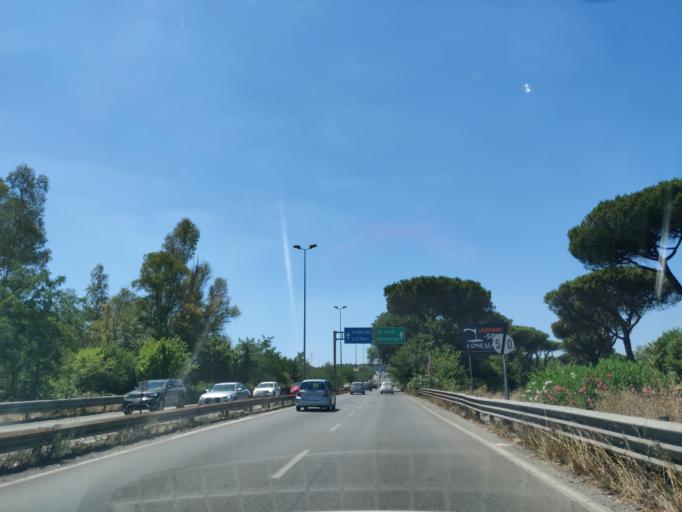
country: IT
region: Latium
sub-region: Citta metropolitana di Roma Capitale
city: Selcetta
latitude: 41.8122
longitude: 12.4594
